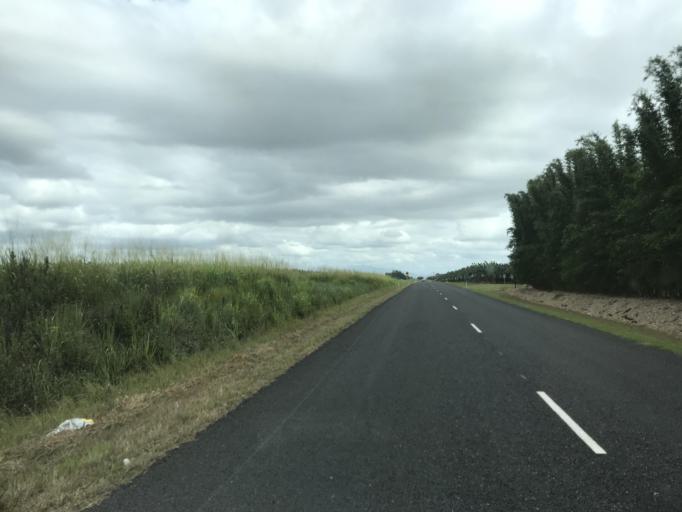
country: AU
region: Queensland
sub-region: Cassowary Coast
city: Innisfail
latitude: -17.6168
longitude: 146.0162
